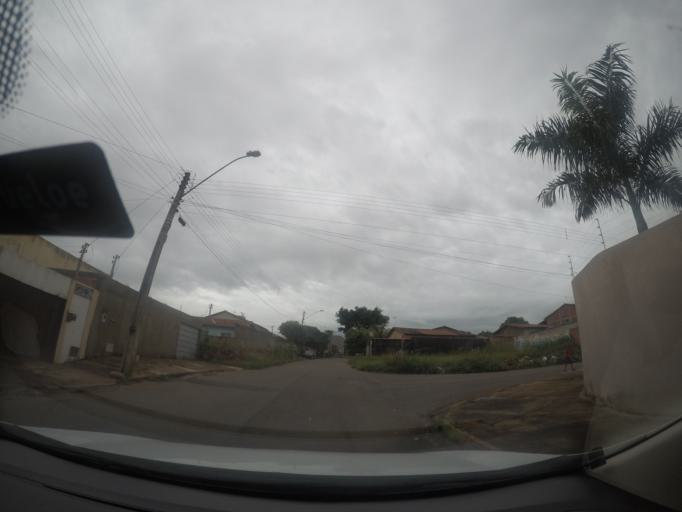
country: BR
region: Goias
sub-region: Goiania
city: Goiania
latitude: -16.6136
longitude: -49.3084
